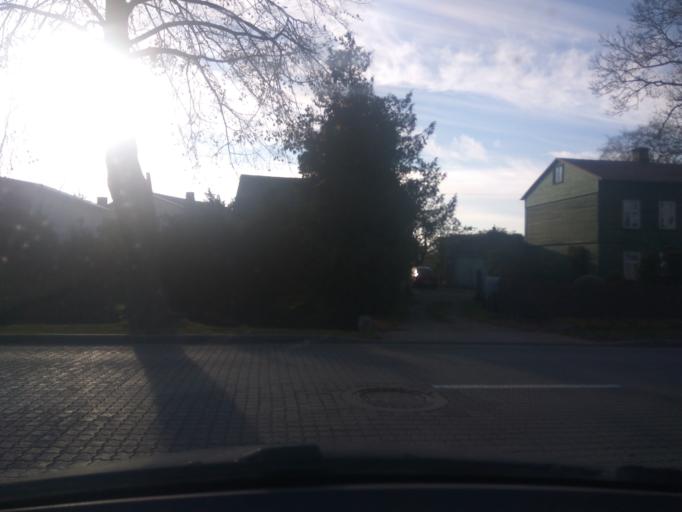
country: LV
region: Ventspils
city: Ventspils
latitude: 57.3792
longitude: 21.5720
